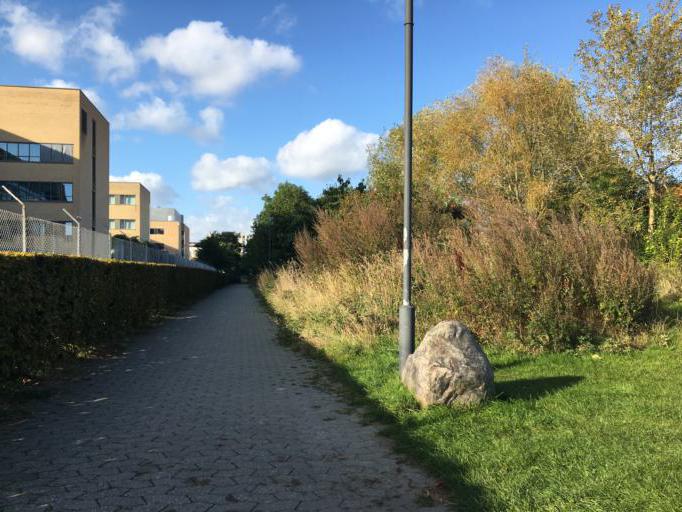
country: DK
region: Capital Region
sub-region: Frederiksberg Kommune
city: Frederiksberg
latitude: 55.6553
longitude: 12.5176
